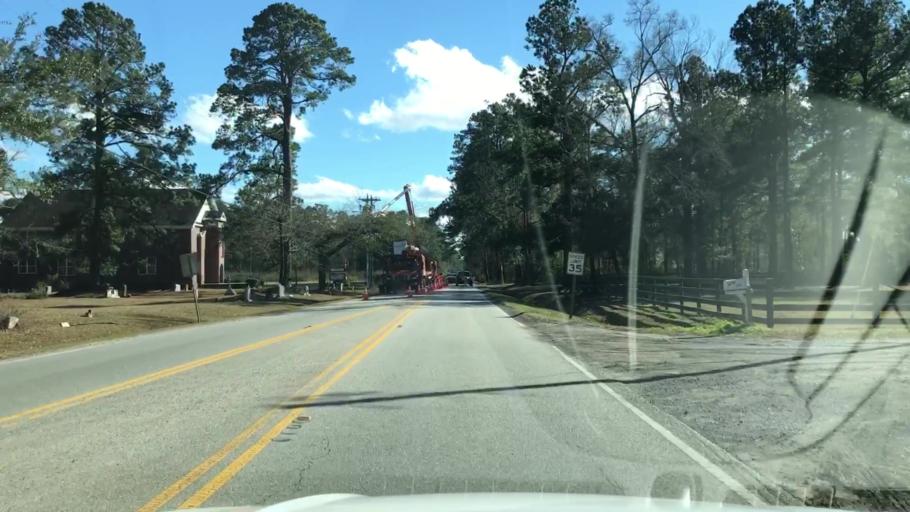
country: US
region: South Carolina
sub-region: Dorchester County
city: Summerville
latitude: 33.0336
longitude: -80.2462
